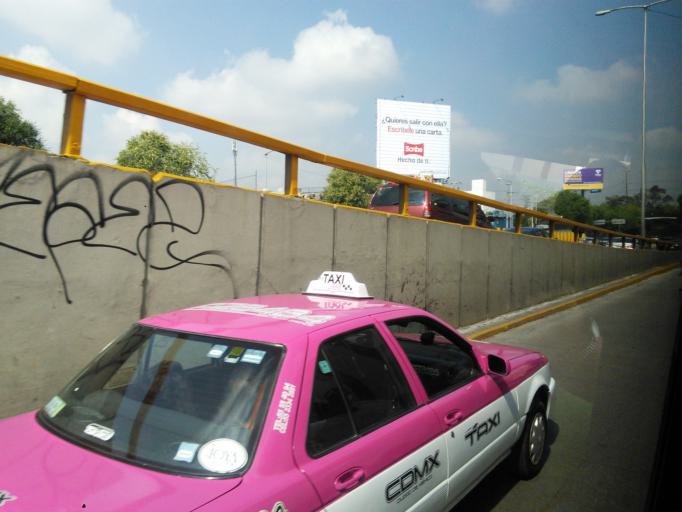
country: MX
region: Mexico City
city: Cuauhtemoc
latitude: 19.4655
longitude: -99.1386
